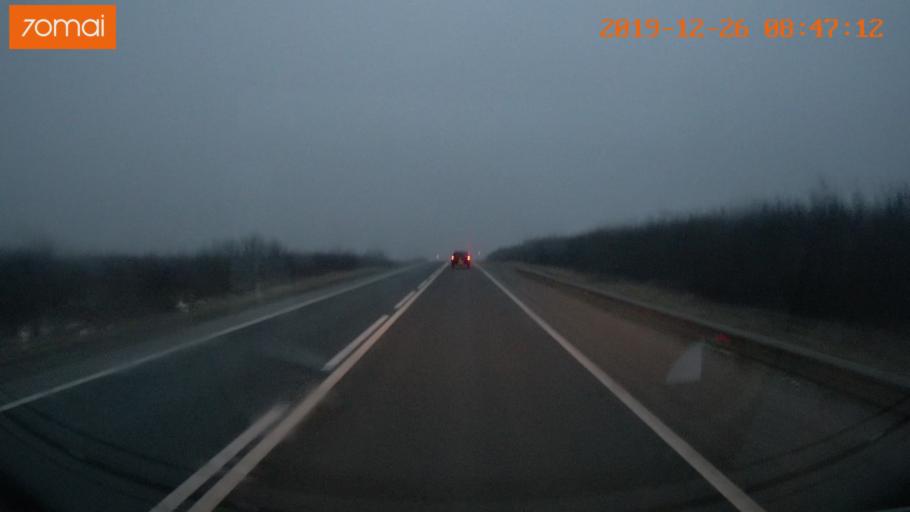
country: RU
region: Jaroslavl
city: Prechistoye
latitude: 58.6202
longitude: 40.3327
